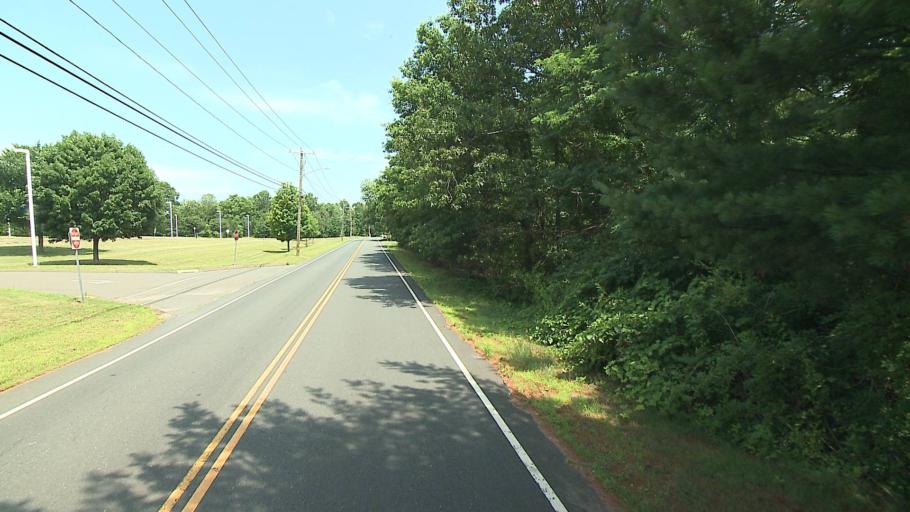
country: US
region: Connecticut
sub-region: Hartford County
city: Suffield Depot
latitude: 41.9794
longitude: -72.6912
